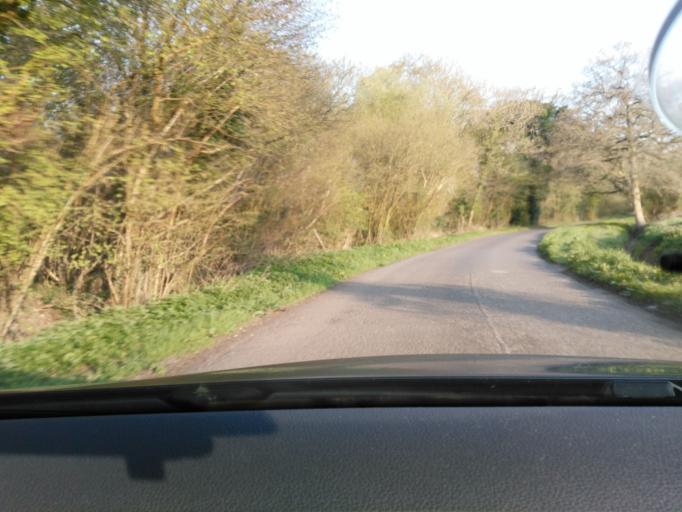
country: GB
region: England
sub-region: West Berkshire
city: Stratfield Mortimer
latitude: 51.3399
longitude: -1.0660
